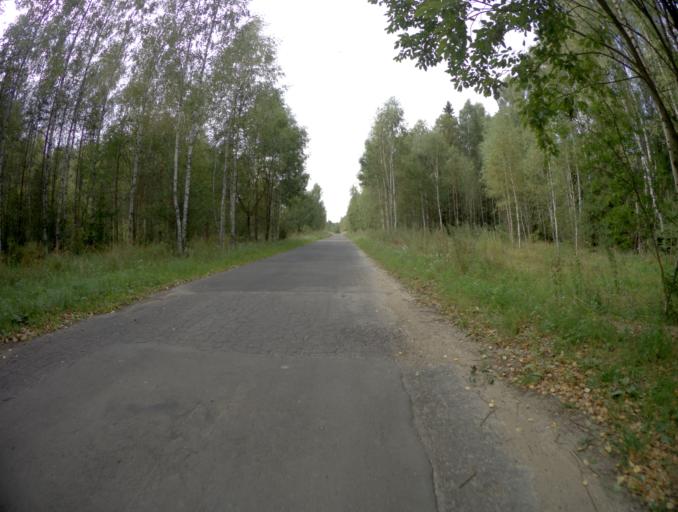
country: RU
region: Vladimir
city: Golovino
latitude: 55.9695
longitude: 40.3997
